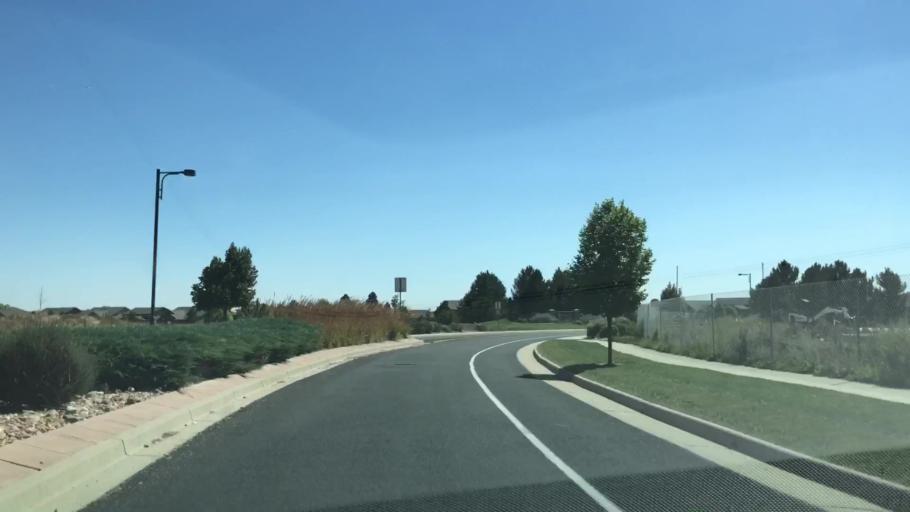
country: US
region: Colorado
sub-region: Larimer County
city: Loveland
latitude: 40.4013
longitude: -104.9825
